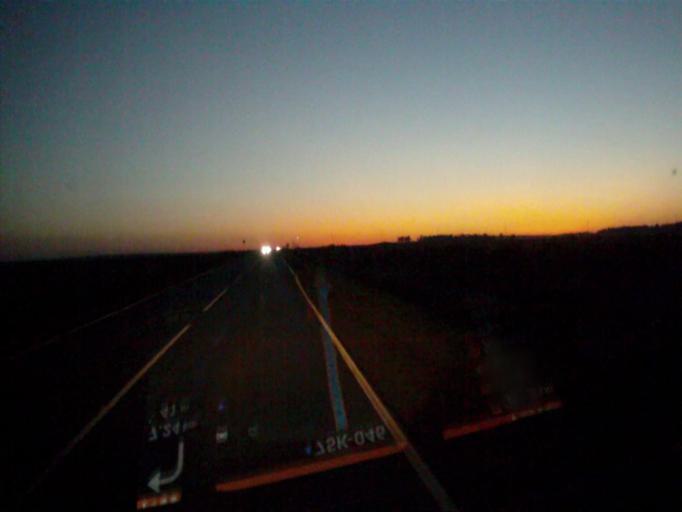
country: RU
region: Chelyabinsk
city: Chebarkul'
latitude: 55.2205
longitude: 60.5626
